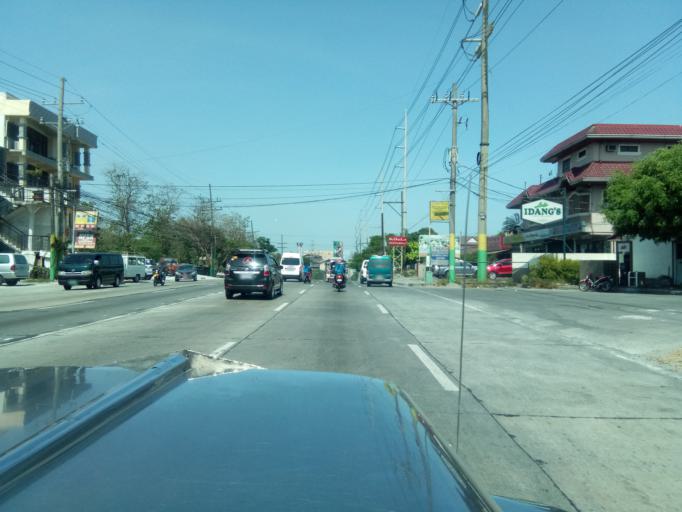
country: PH
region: Calabarzon
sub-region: Province of Cavite
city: Dasmarinas
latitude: 14.2986
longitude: 120.9493
